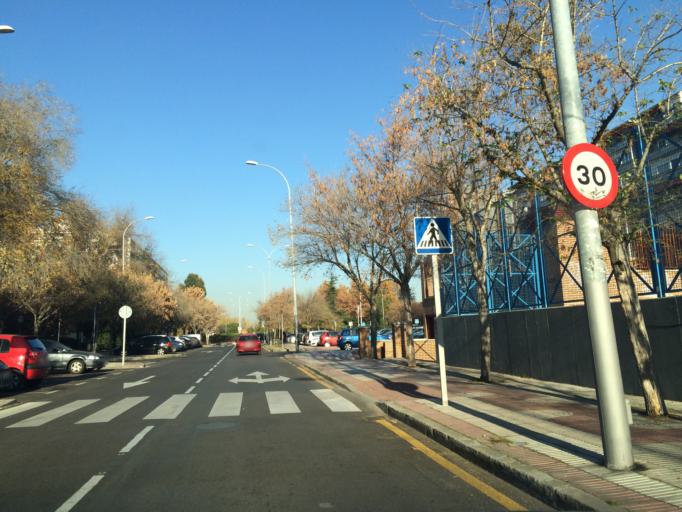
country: ES
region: Madrid
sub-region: Provincia de Madrid
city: Alcorcon
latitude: 40.3545
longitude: -3.8113
